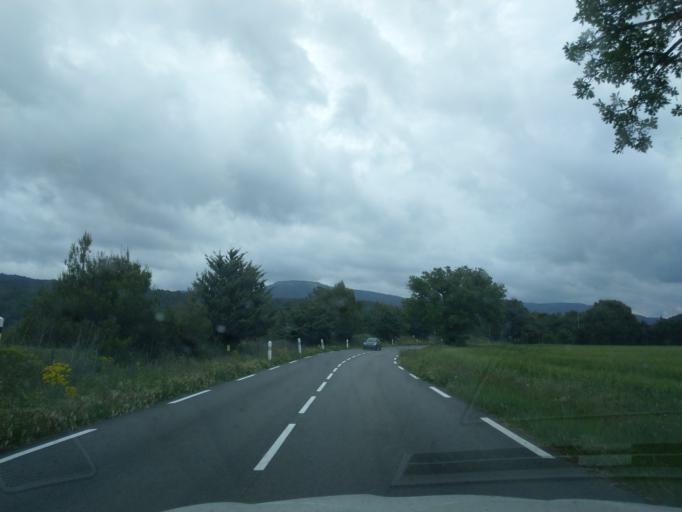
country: FR
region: Provence-Alpes-Cote d'Azur
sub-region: Departement du Var
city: Signes
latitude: 43.2831
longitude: 5.8284
